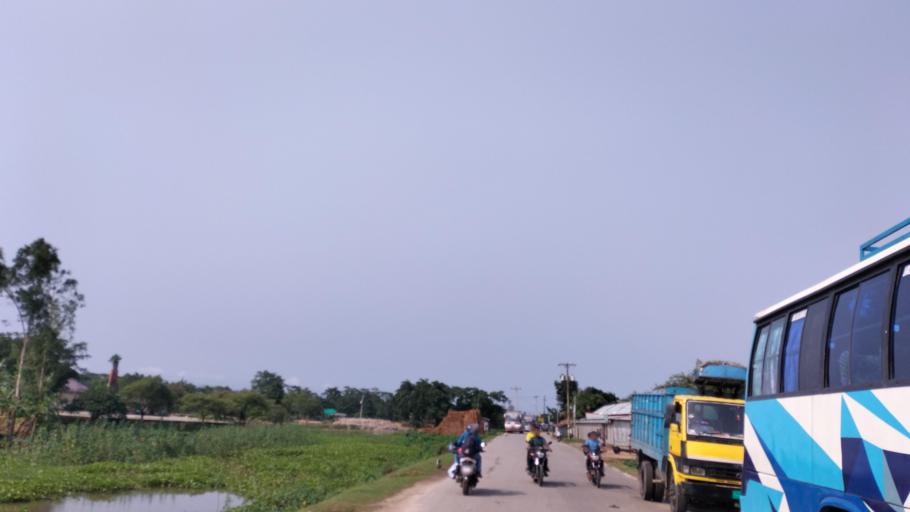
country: BD
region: Dhaka
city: Netrakona
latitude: 25.0697
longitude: 90.8847
